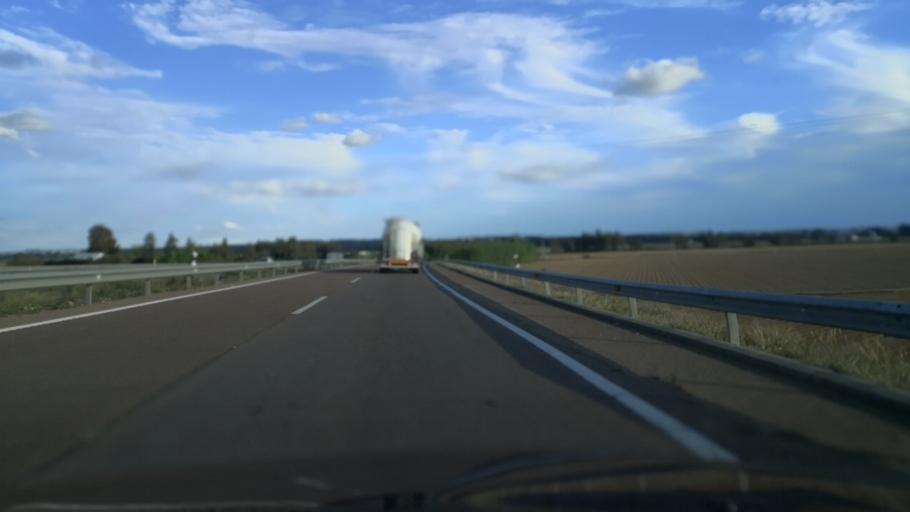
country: ES
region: Extremadura
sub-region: Provincia de Badajoz
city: Badajoz
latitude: 38.9161
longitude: -6.9519
